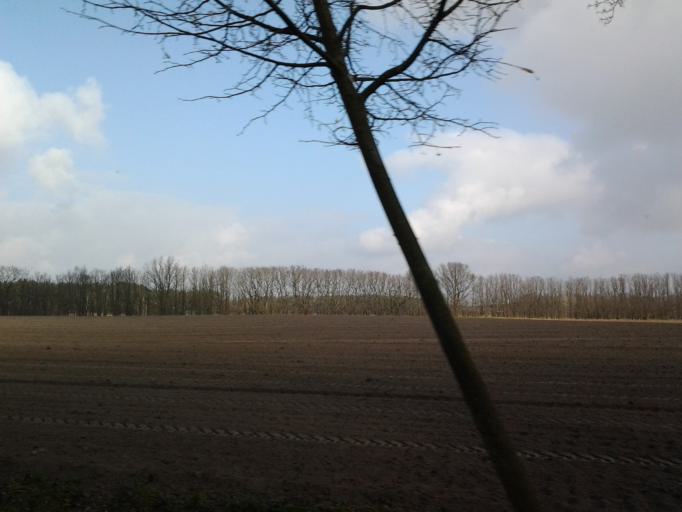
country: DE
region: Berlin
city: Staaken
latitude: 52.5097
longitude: 13.1312
